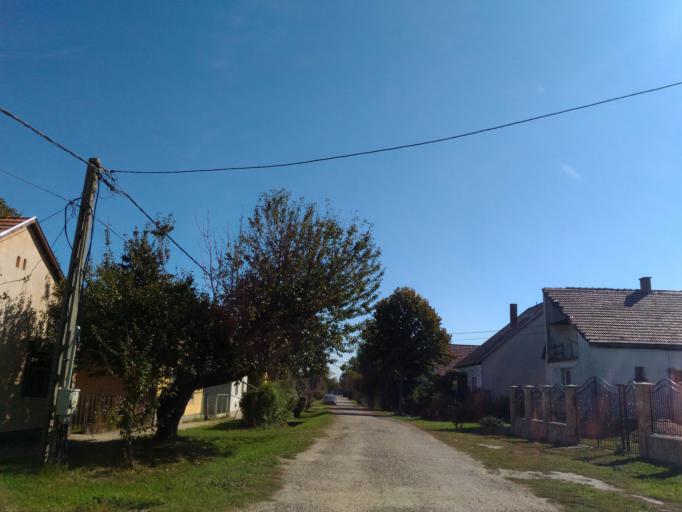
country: HU
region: Fejer
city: Ivancsa
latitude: 47.1806
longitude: 18.8203
